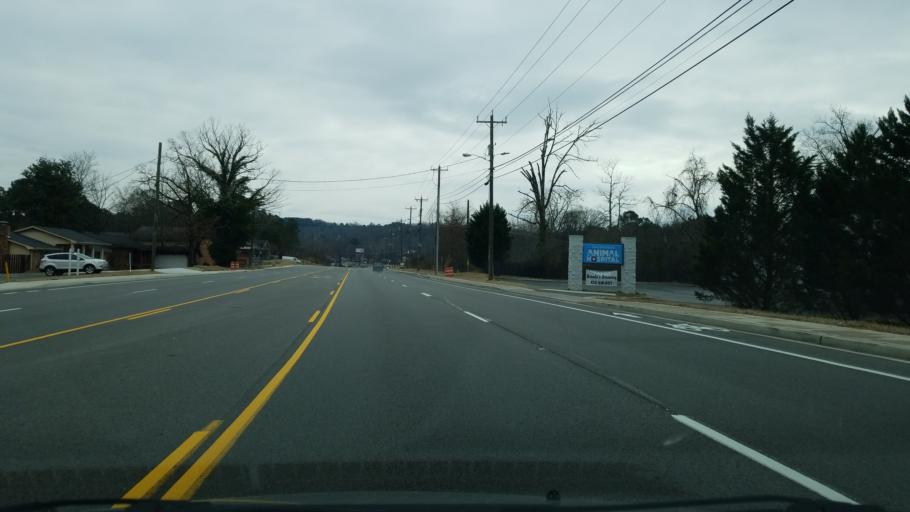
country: US
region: Tennessee
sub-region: Hamilton County
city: East Brainerd
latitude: 35.0017
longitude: -85.1388
